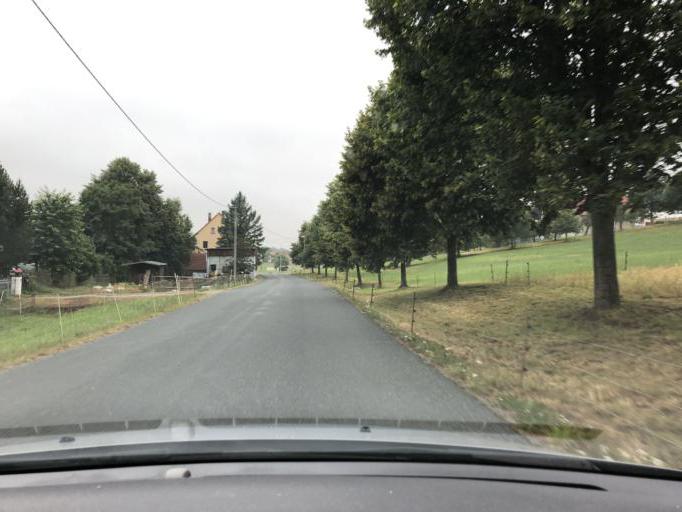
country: DE
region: Thuringia
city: Langenleuba-Niederhain
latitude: 50.9967
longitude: 12.6265
